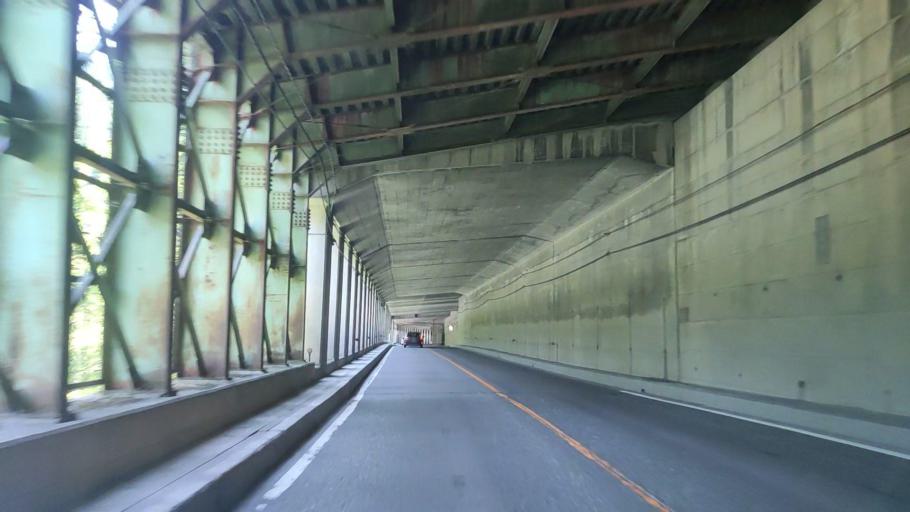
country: JP
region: Niigata
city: Itoigawa
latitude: 36.9122
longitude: 137.8629
